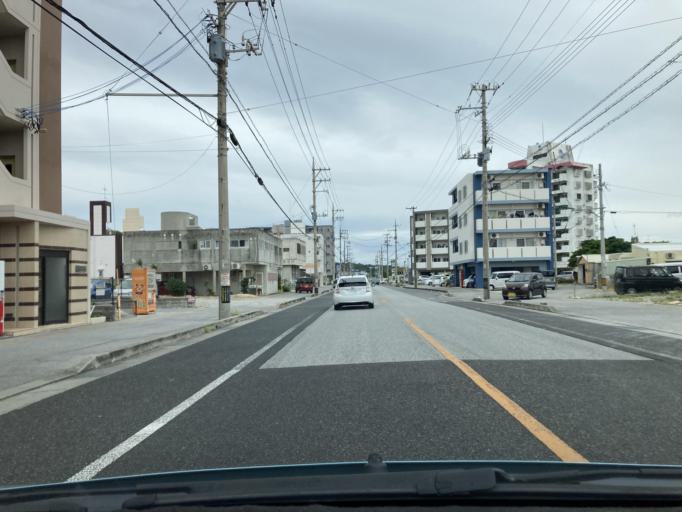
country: JP
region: Okinawa
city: Itoman
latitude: 26.1213
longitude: 127.6696
